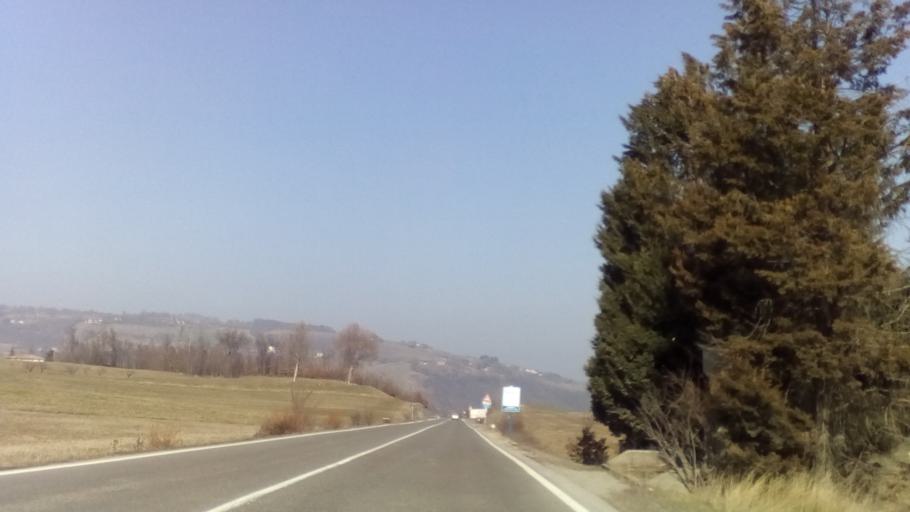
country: IT
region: Emilia-Romagna
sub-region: Provincia di Modena
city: Sant'Antonio
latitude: 44.3914
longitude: 10.8190
